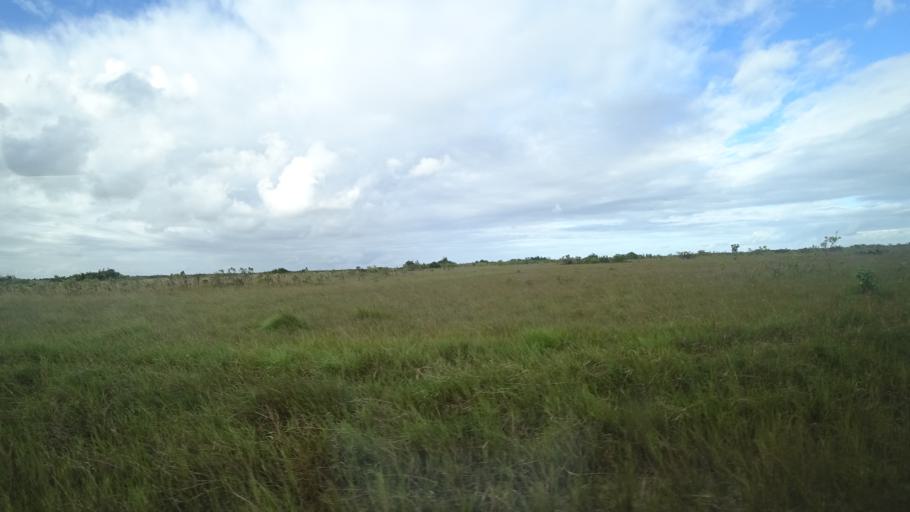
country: MZ
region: Sofala
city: Beira
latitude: -19.6725
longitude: 35.0589
